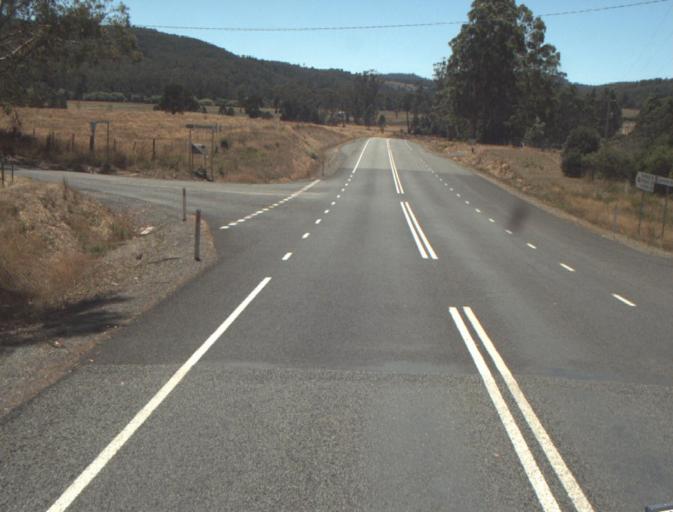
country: AU
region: Tasmania
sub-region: Launceston
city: Newstead
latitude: -41.3347
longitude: 147.3483
